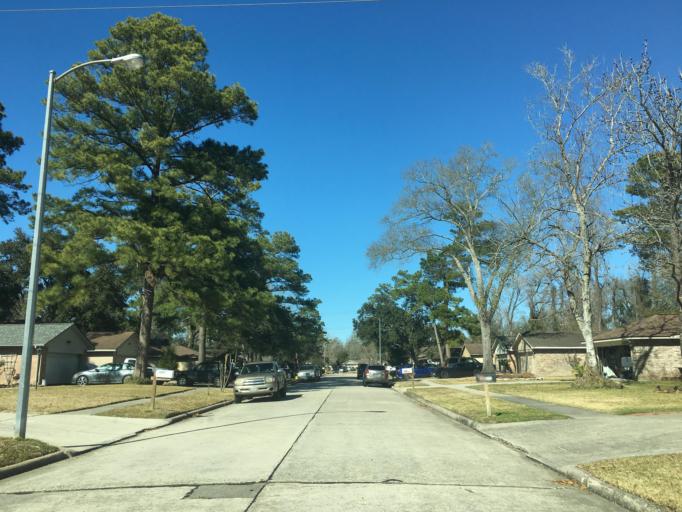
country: US
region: Texas
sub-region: Harris County
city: Spring
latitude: 30.0870
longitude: -95.4660
